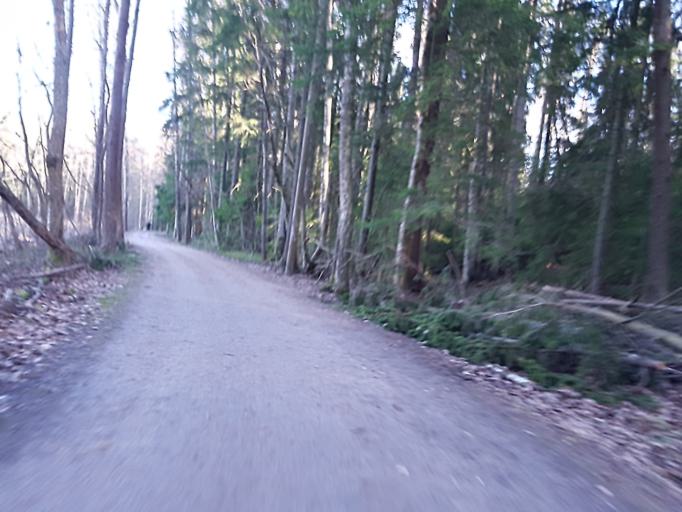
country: FI
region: Uusimaa
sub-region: Helsinki
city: Helsinki
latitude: 60.2694
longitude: 24.9343
